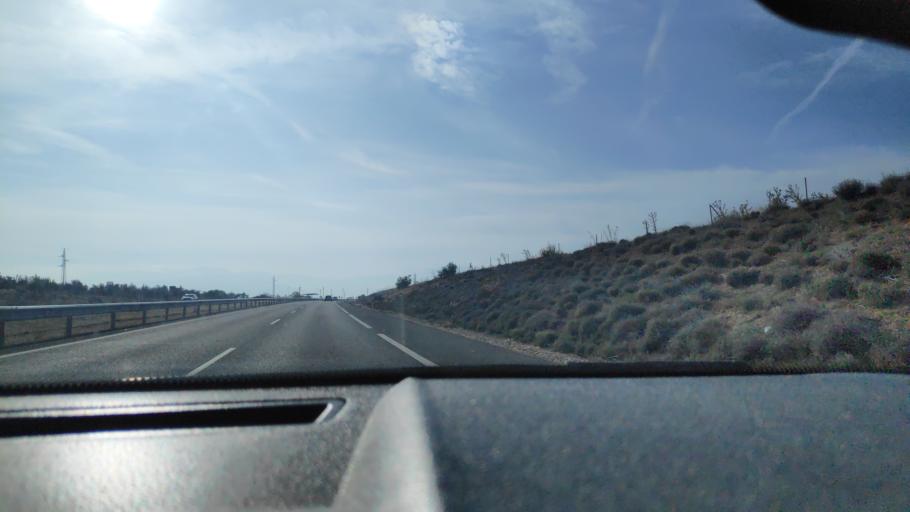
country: ES
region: Andalusia
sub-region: Provincia de Jaen
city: Jaen
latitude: 37.8476
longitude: -3.7642
